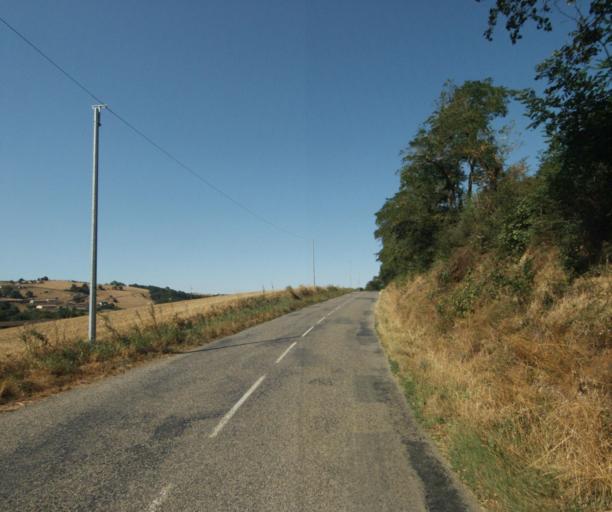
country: FR
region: Rhone-Alpes
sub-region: Departement du Rhone
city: Courzieu
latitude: 45.7546
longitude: 4.5613
